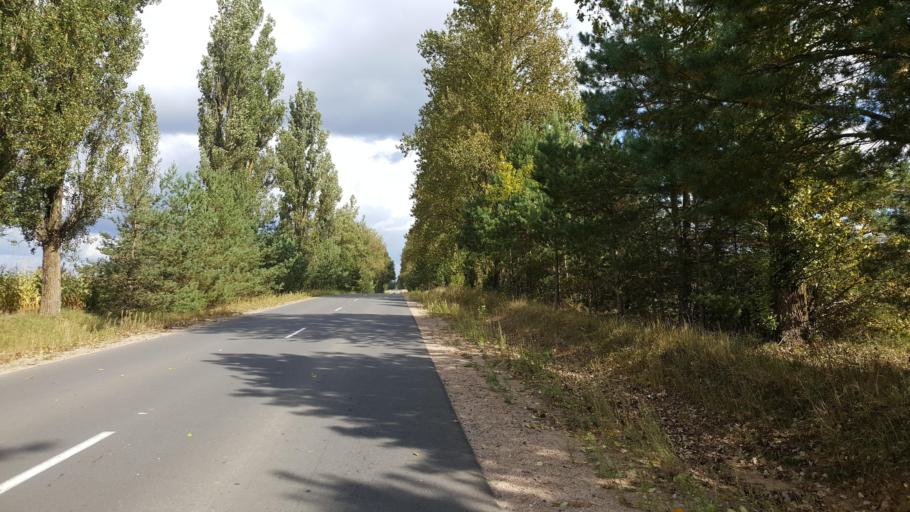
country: BY
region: Brest
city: Kamyanyets
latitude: 52.4079
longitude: 23.9116
